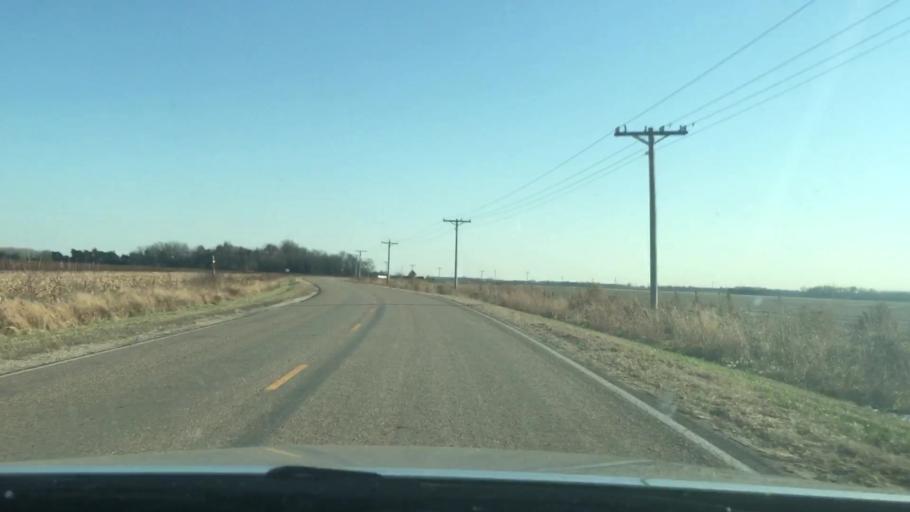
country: US
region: Kansas
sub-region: Reno County
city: Nickerson
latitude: 38.2655
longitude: -98.0906
